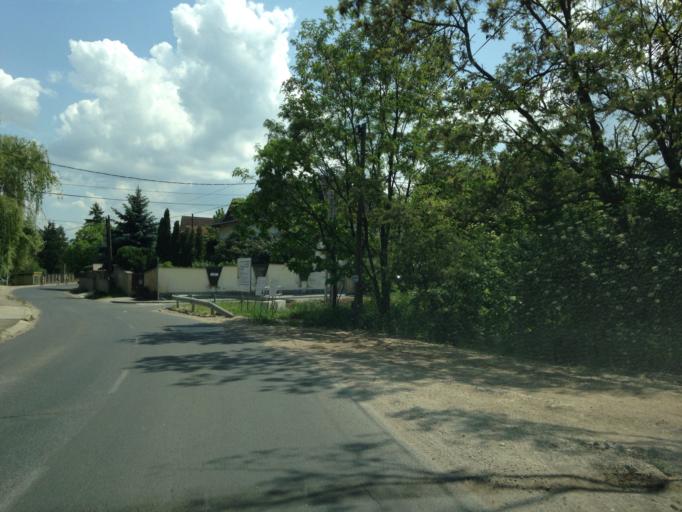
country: HU
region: Pest
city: Szentendre
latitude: 47.6810
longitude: 19.0628
